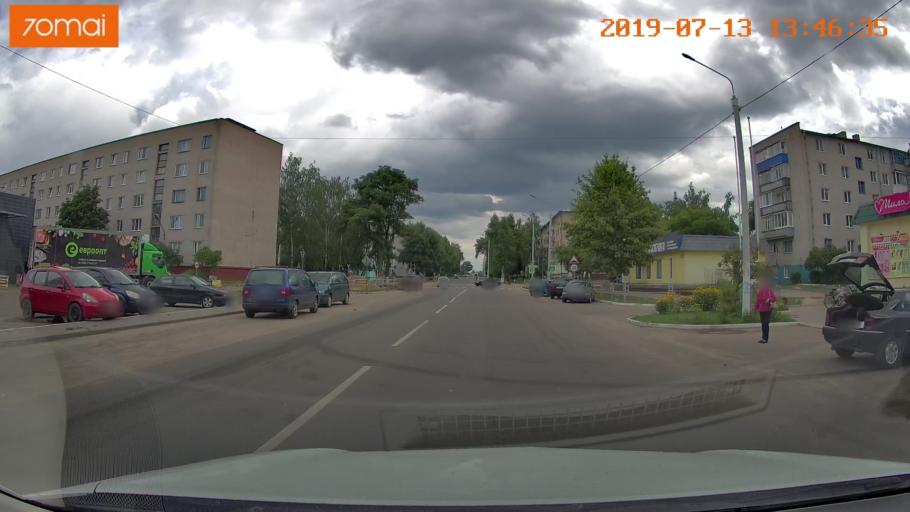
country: BY
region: Mogilev
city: Asipovichy
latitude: 53.2953
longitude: 28.6351
